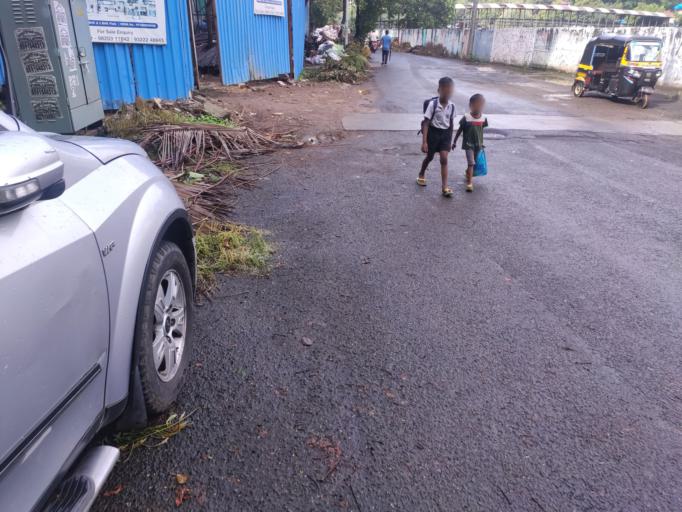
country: IN
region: Maharashtra
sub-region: Mumbai Suburban
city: Borivli
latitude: 19.2466
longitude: 72.8576
